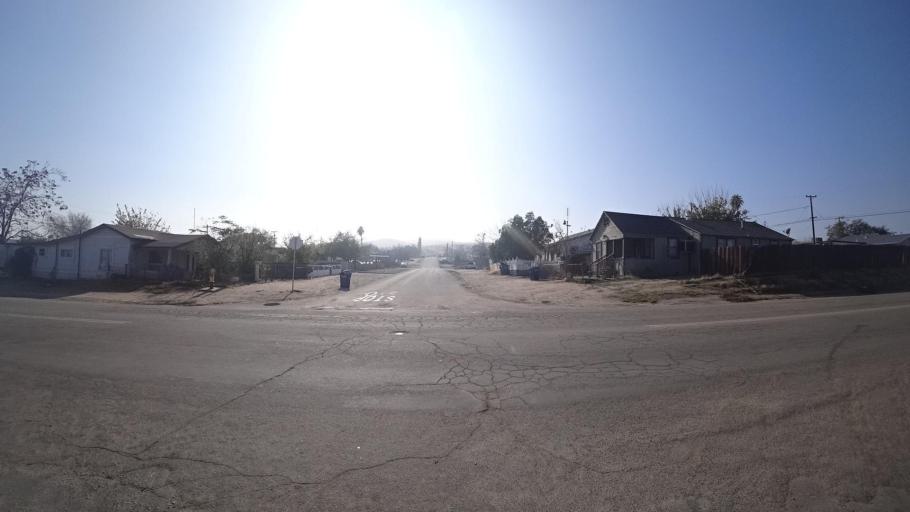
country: US
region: California
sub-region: Kern County
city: South Taft
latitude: 35.1332
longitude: -119.4623
